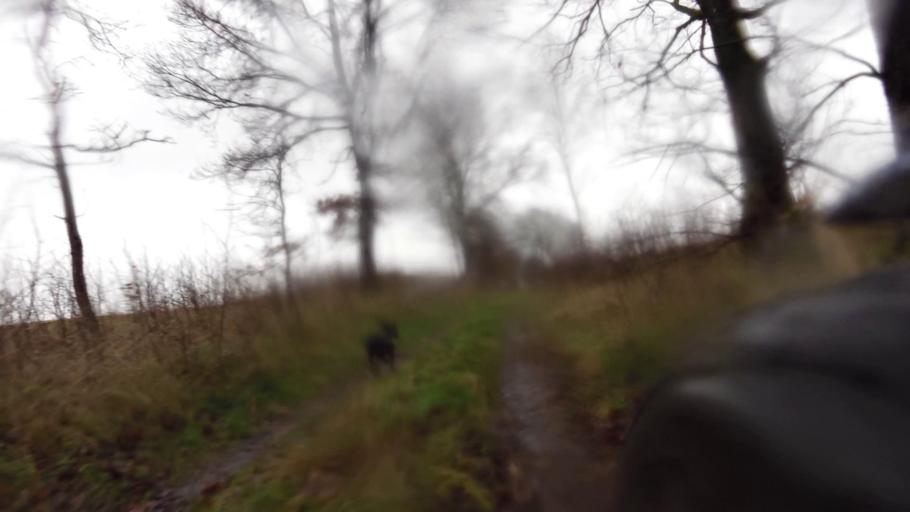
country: PL
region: West Pomeranian Voivodeship
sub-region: Powiat drawski
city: Drawsko Pomorskie
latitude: 53.5570
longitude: 15.8383
